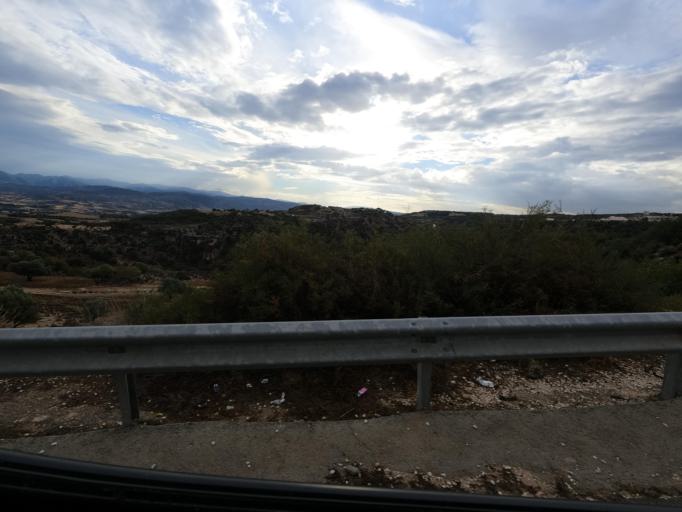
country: CY
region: Pafos
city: Polis
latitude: 35.0056
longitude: 32.3905
